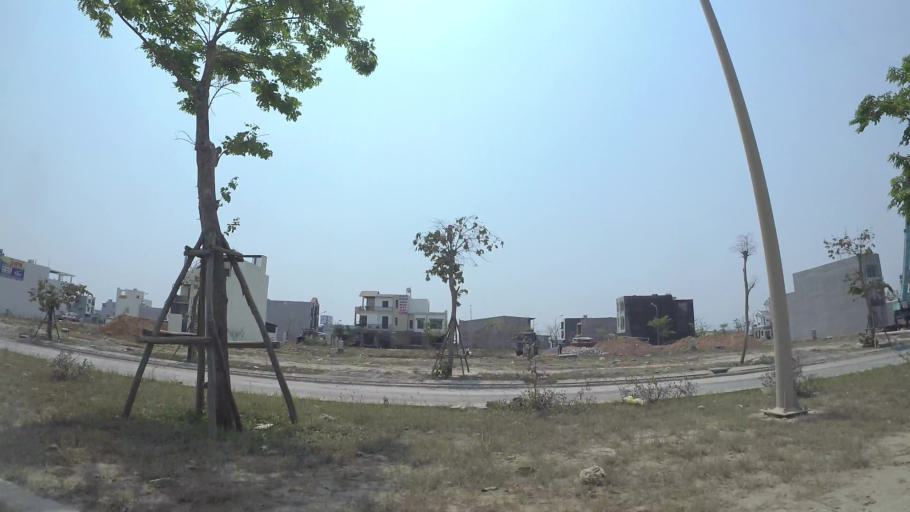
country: VN
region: Da Nang
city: Ngu Hanh Son
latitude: 16.0118
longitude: 108.2393
